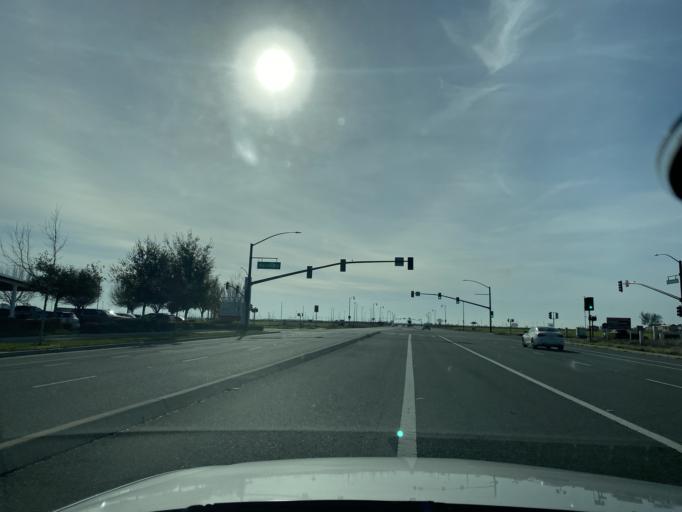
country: US
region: California
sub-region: Sacramento County
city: Elk Grove
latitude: 38.3846
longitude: -121.3728
